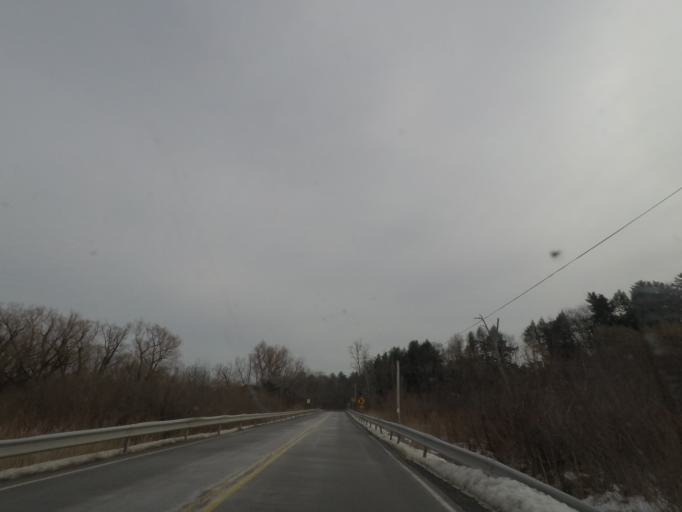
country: US
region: New York
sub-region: Albany County
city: Voorheesville
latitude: 42.6631
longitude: -73.9852
